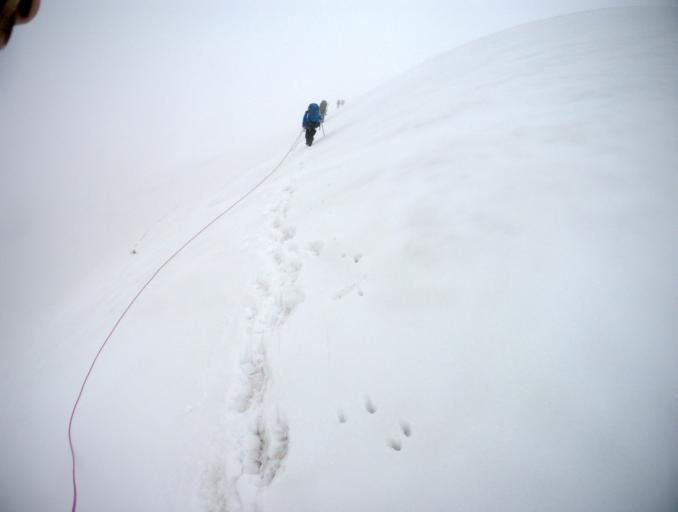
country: RU
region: Kabardino-Balkariya
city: Terskol
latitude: 43.3805
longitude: 42.4667
